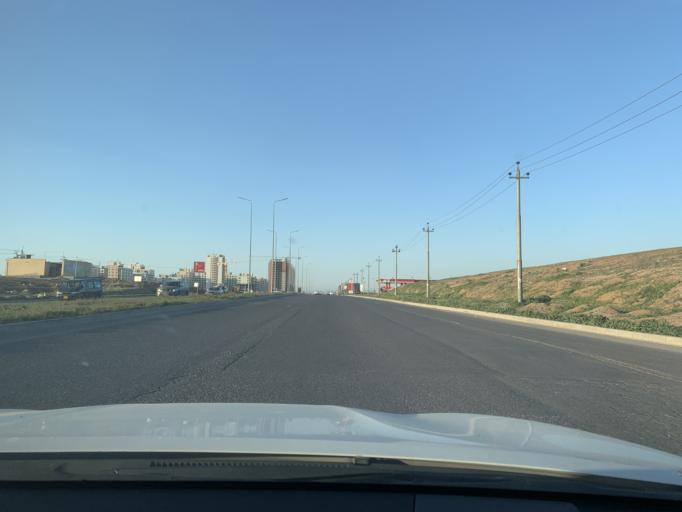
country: IQ
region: Arbil
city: Erbil
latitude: 36.2521
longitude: 44.0136
